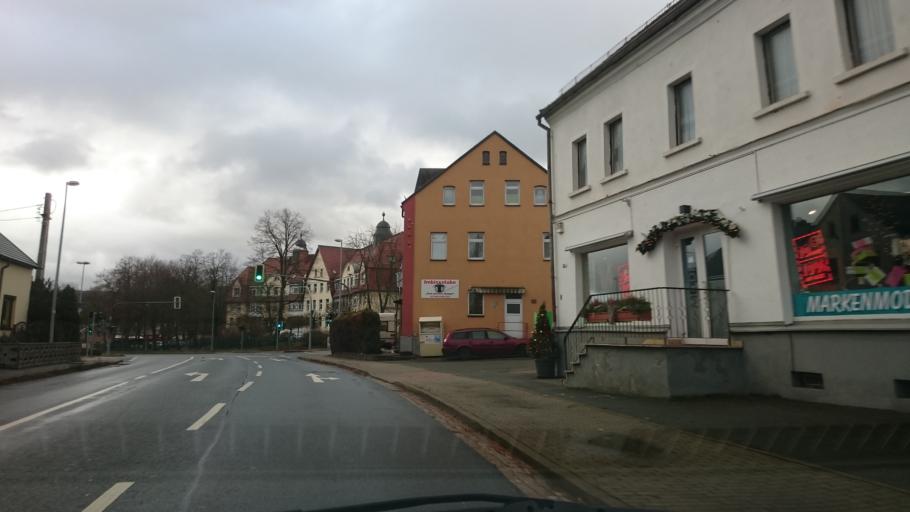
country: DE
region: Saxony
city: Kirchberg
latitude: 50.6500
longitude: 12.5594
